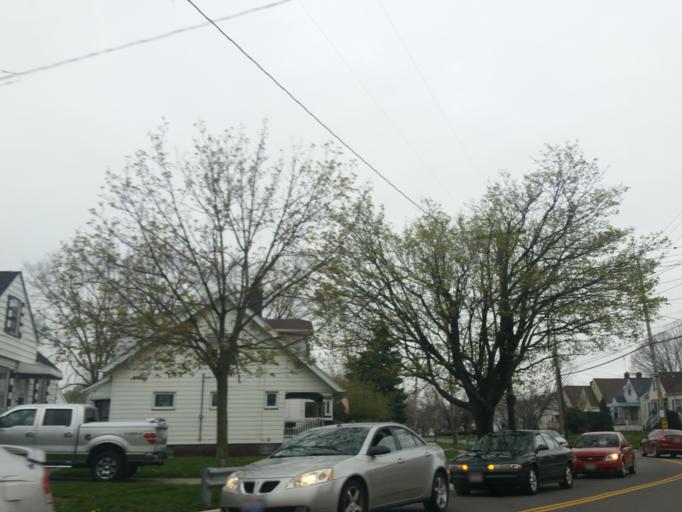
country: US
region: Ohio
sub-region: Cuyahoga County
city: Brooklyn
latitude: 41.4300
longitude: -81.7240
